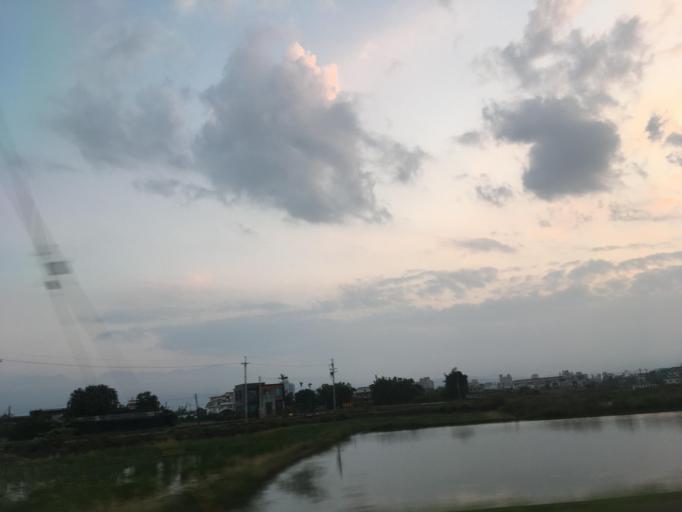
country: TW
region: Taiwan
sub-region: Yilan
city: Yilan
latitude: 24.6914
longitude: 121.7838
